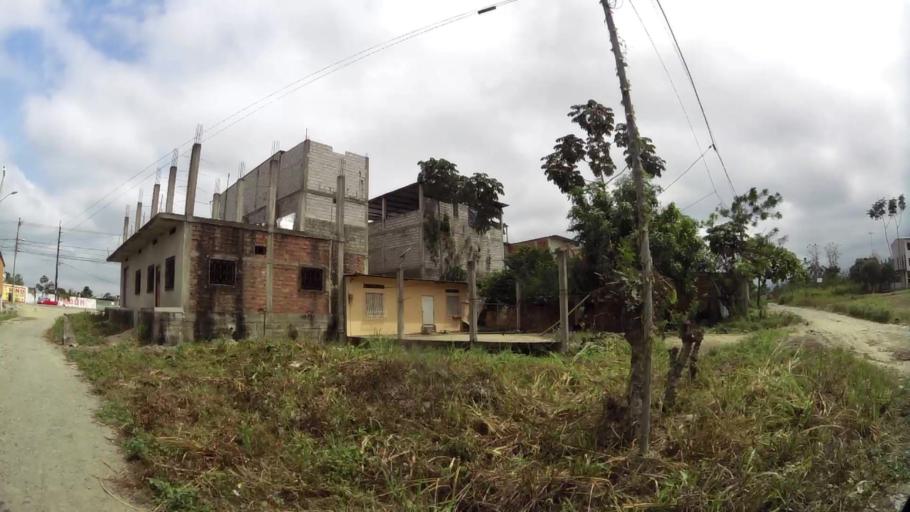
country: EC
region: Guayas
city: Naranjal
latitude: -2.6842
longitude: -79.6251
